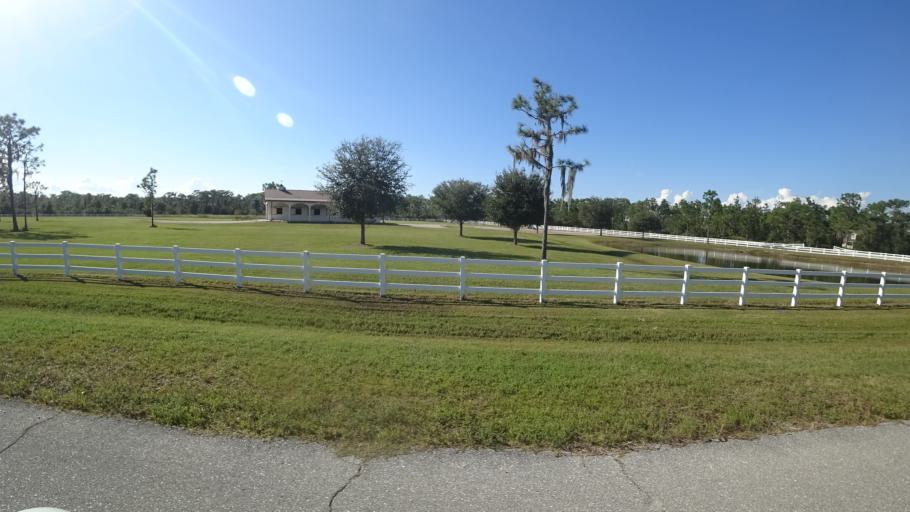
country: US
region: Florida
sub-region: Sarasota County
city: Lake Sarasota
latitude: 27.3967
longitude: -82.2838
